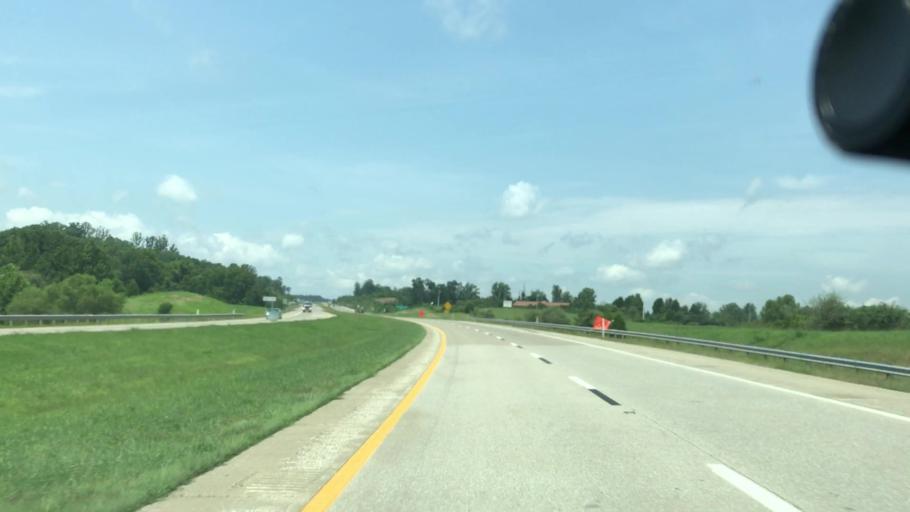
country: US
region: West Virginia
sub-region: Putnam County
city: Eleanor
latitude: 38.5470
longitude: -81.9753
